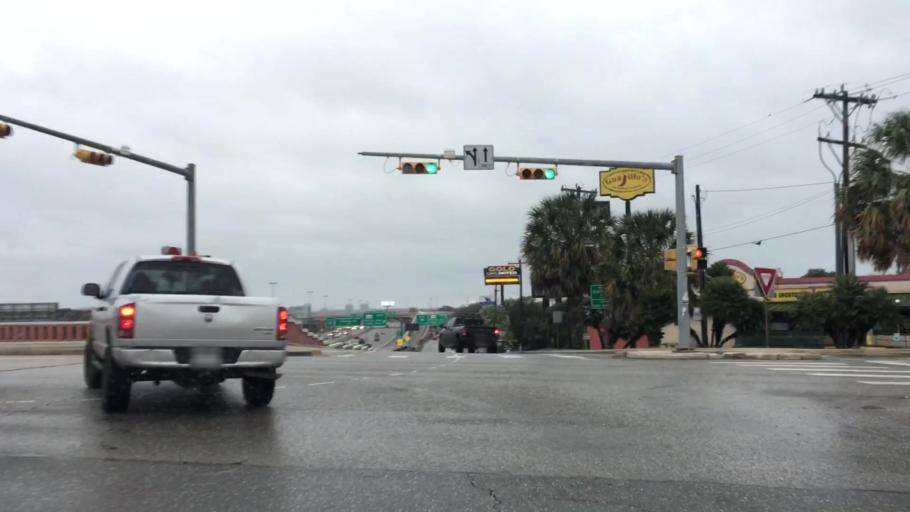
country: US
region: Texas
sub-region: Bexar County
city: Castle Hills
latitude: 29.5209
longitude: -98.5065
